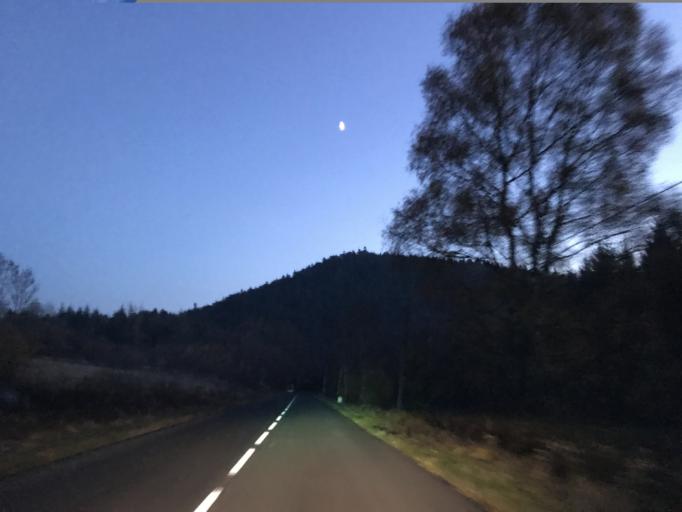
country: FR
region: Rhone-Alpes
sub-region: Departement de la Loire
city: Noiretable
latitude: 45.7702
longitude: 3.6820
